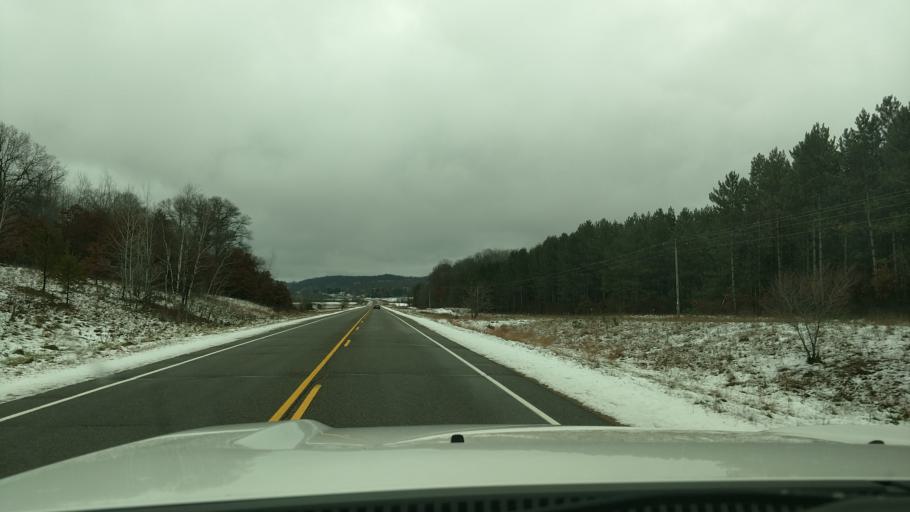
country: US
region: Wisconsin
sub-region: Dunn County
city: Tainter Lake
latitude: 45.1243
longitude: -91.8668
